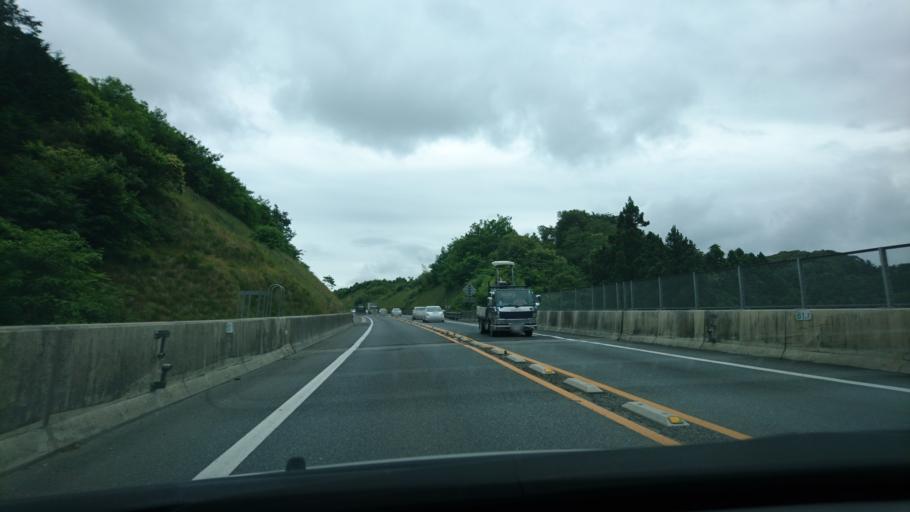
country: JP
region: Miyagi
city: Wakuya
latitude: 38.6417
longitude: 141.2642
